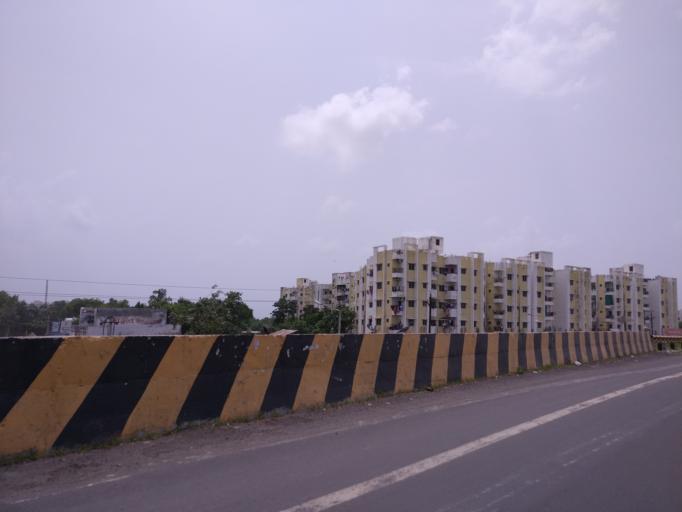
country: IN
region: Gujarat
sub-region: Mahesana
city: Jhulasan
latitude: 23.2411
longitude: 72.4883
